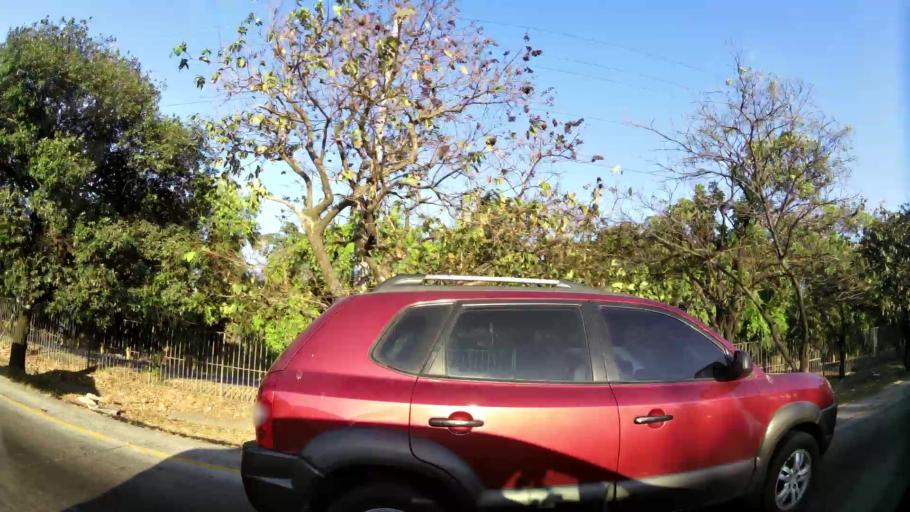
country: SV
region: La Libertad
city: Santa Tecla
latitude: 13.7297
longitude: -89.3590
